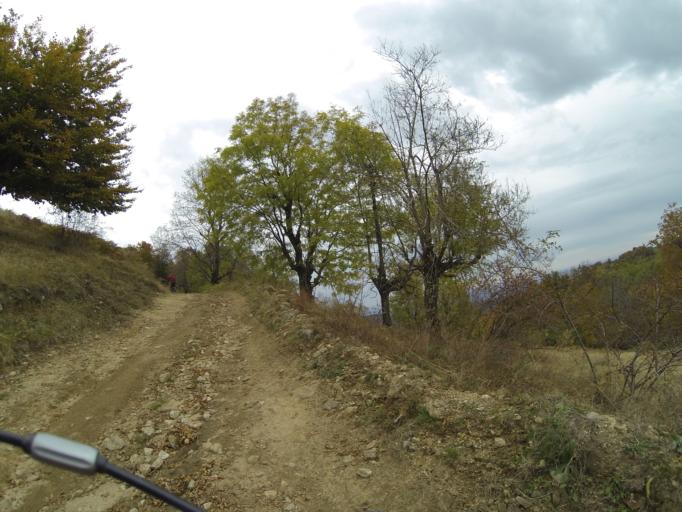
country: RO
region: Gorj
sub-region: Comuna Pades
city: Closani
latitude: 45.1123
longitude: 22.8480
